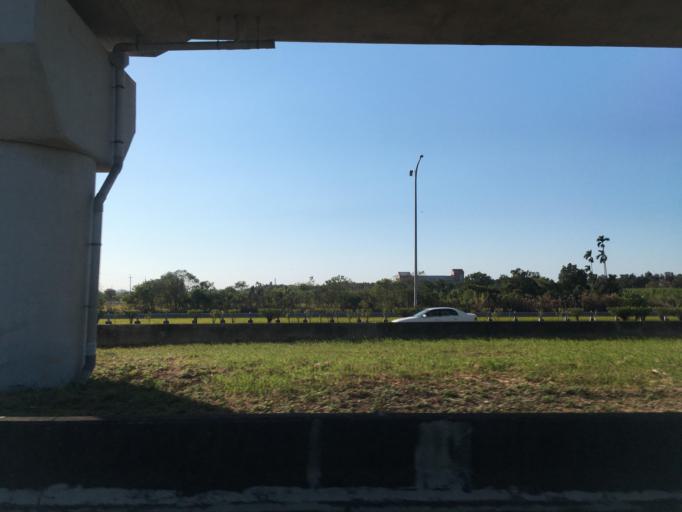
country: TW
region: Taiwan
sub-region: Chiayi
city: Taibao
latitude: 23.4497
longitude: 120.3235
